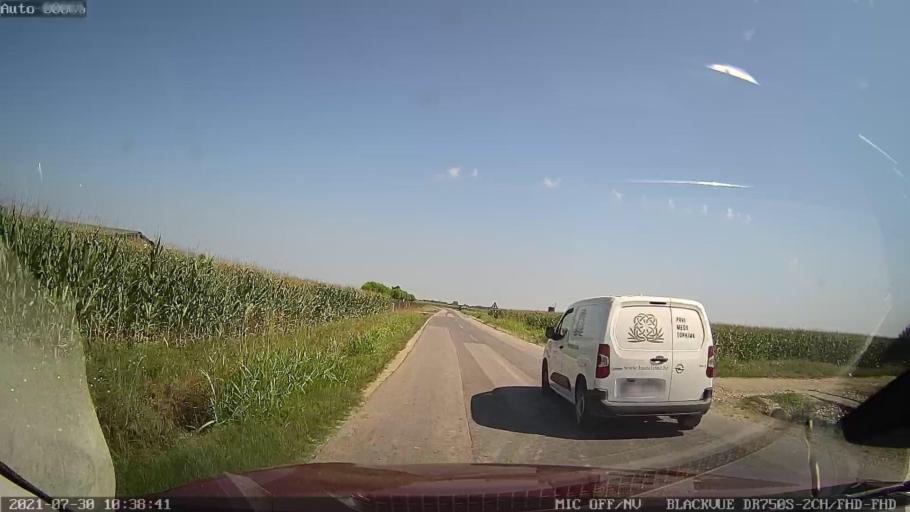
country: HR
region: Varazdinska
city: Jalzabet
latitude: 46.2622
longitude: 16.4344
